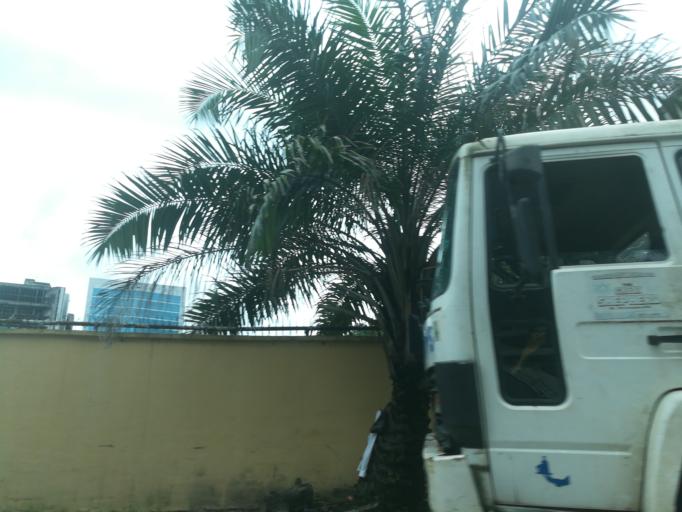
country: NG
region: Lagos
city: Ikoyi
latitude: 6.4322
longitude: 3.4168
